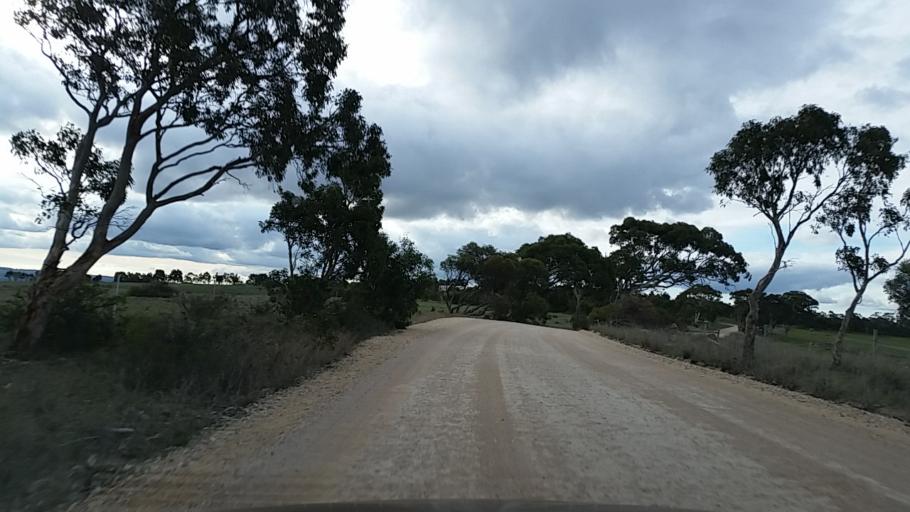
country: AU
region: South Australia
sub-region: Mount Barker
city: Callington
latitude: -34.9903
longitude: 139.0568
